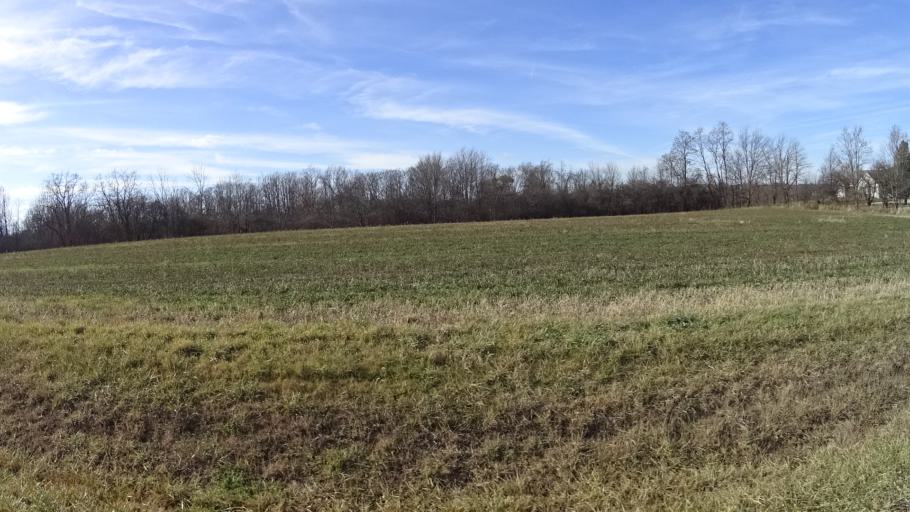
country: US
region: Ohio
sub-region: Lorain County
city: Wellington
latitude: 41.0702
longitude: -82.2395
